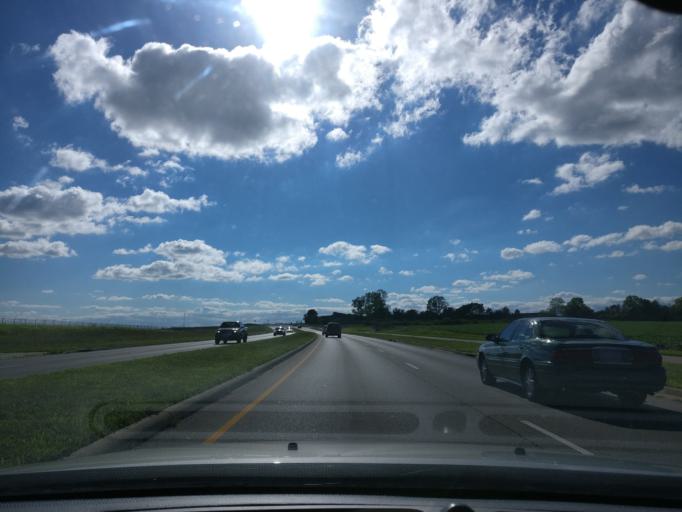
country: US
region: Ohio
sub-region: Warren County
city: Five Points
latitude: 39.5972
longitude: -84.2187
